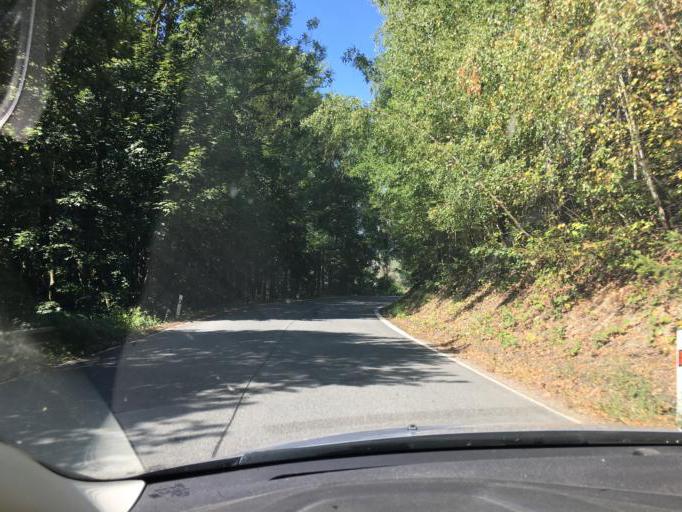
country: CZ
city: Plavy
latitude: 50.7037
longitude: 15.3420
